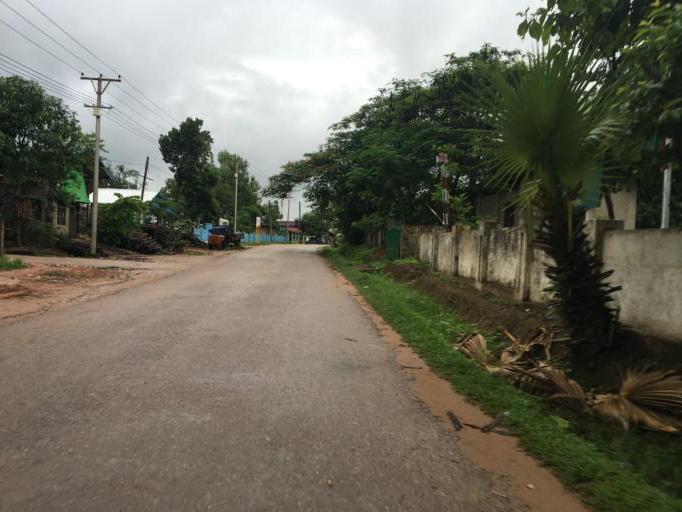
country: MM
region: Mon
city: Mudon
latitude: 16.0439
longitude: 98.1179
